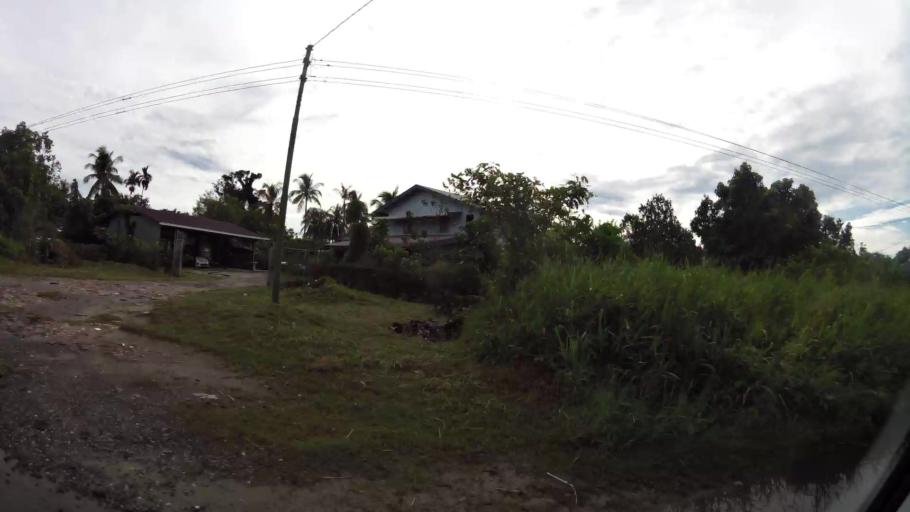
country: BN
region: Belait
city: Seria
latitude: 4.6144
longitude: 114.3508
